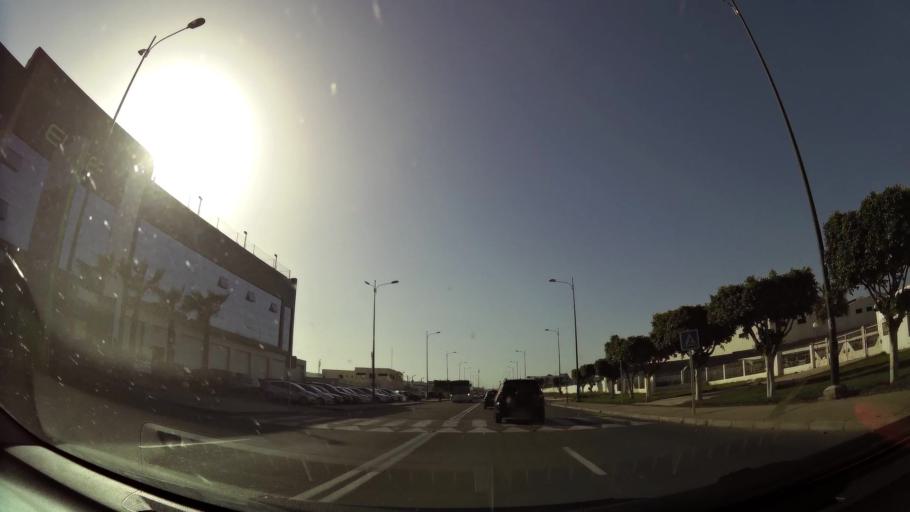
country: MA
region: Souss-Massa-Draa
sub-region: Inezgane-Ait Mellou
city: Inezgane
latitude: 30.3876
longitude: -9.5253
